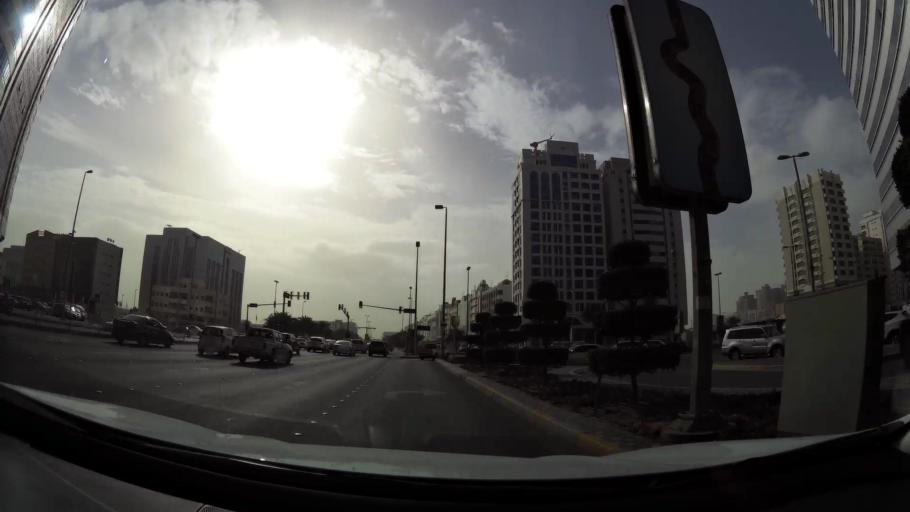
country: AE
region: Abu Dhabi
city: Abu Dhabi
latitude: 24.4836
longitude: 54.3753
